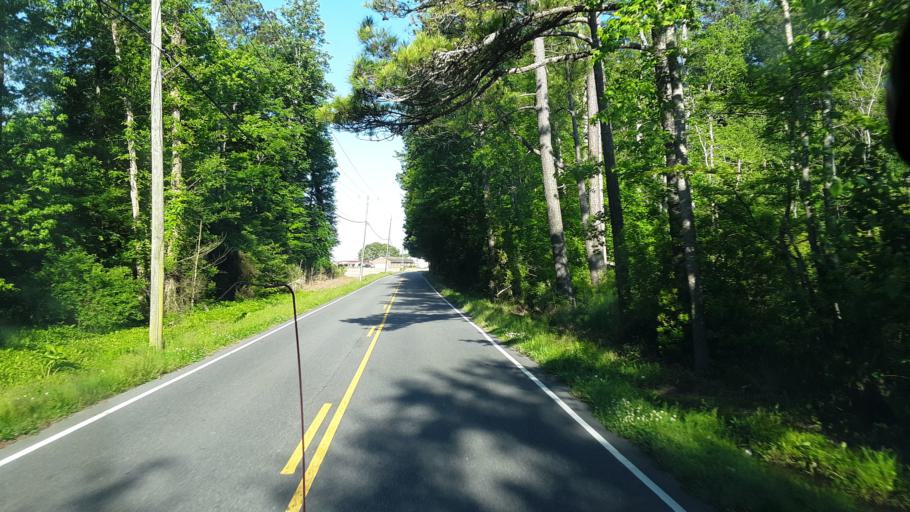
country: US
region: Virginia
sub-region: City of Virginia Beach
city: Virginia Beach
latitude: 36.7204
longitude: -76.0423
